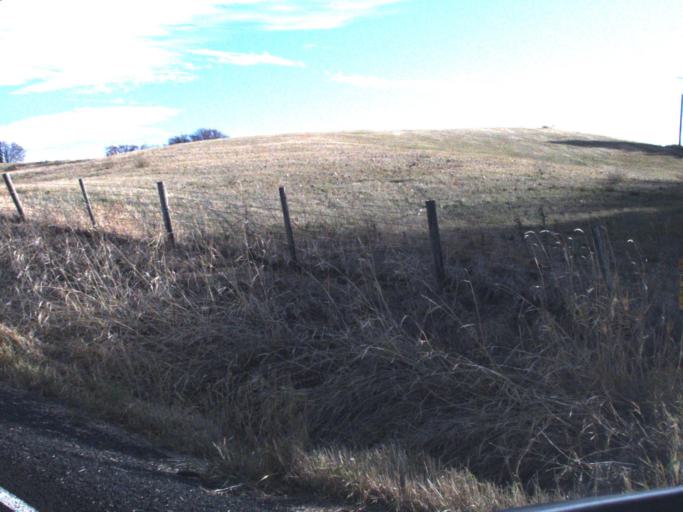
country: US
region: Washington
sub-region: Whitman County
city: Colfax
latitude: 46.9339
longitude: -117.2161
